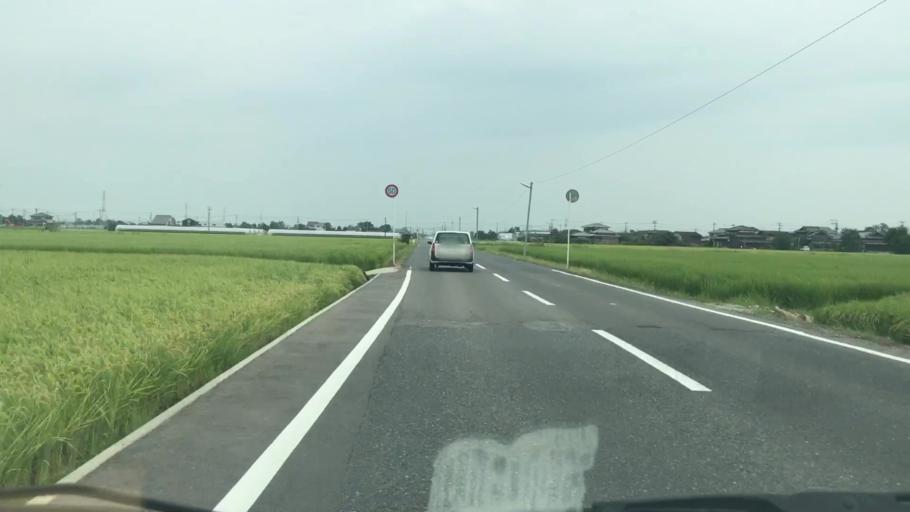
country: JP
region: Saga Prefecture
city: Saga-shi
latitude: 33.2280
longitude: 130.2964
